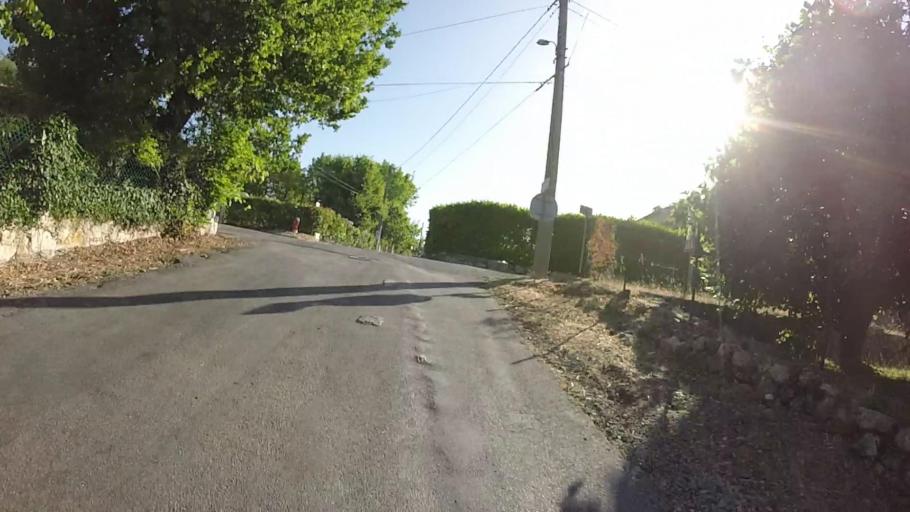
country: FR
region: Provence-Alpes-Cote d'Azur
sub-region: Departement des Alpes-Maritimes
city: Chateauneuf-Grasse
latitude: 43.6705
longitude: 6.9984
